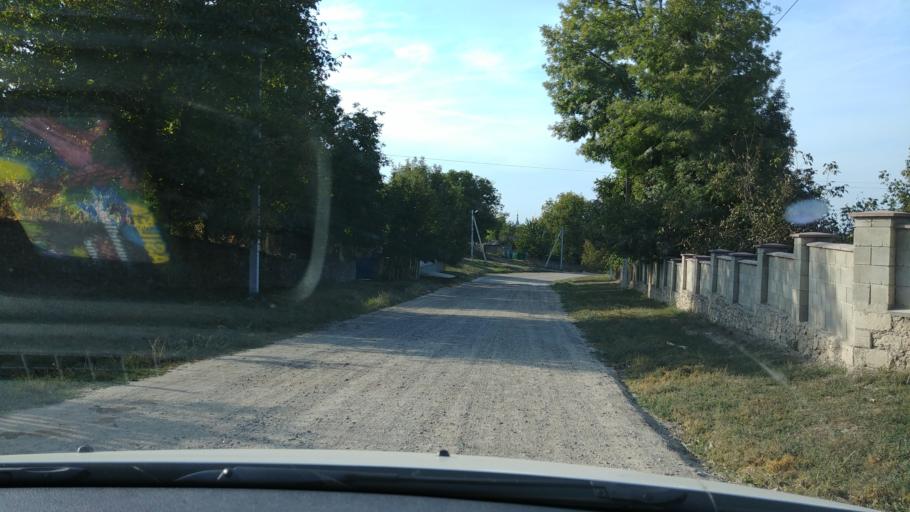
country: MD
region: Rezina
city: Rezina
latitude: 47.7470
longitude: 28.8860
